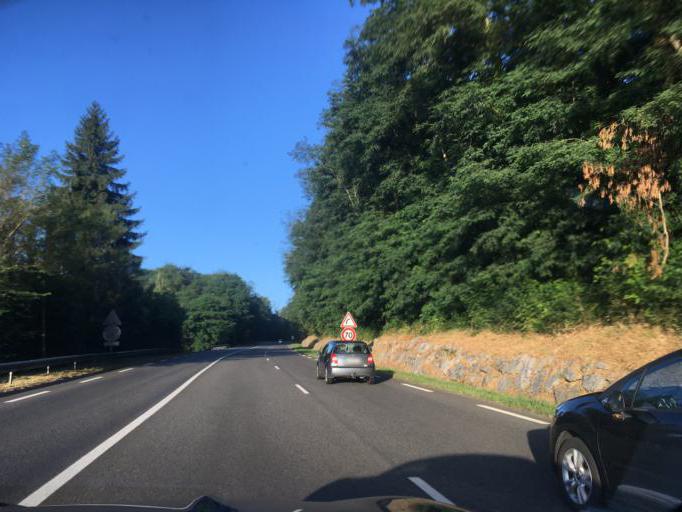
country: FR
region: Midi-Pyrenees
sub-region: Departement des Hautes-Pyrenees
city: Ibos
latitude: 43.2427
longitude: -0.0188
